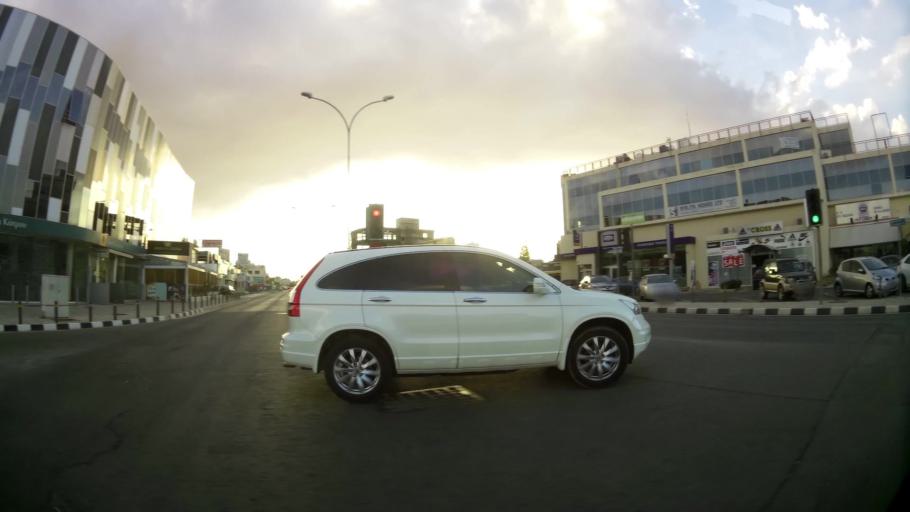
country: CY
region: Lefkosia
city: Tseri
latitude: 35.1226
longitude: 33.3206
